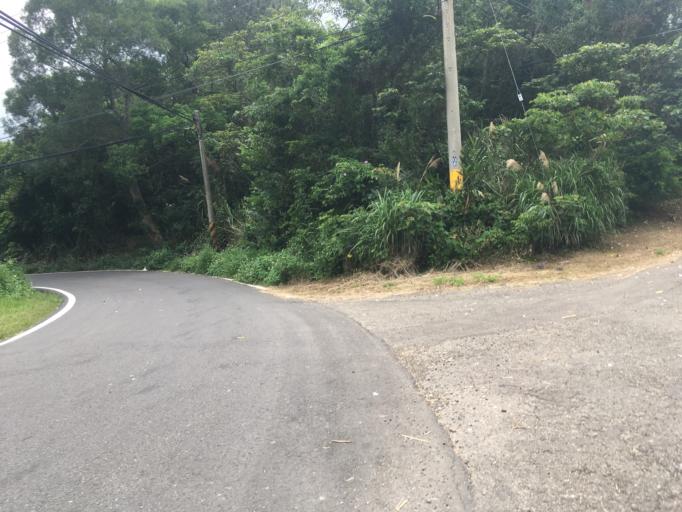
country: TW
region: Taiwan
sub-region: Hsinchu
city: Hsinchu
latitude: 24.7486
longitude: 120.9840
